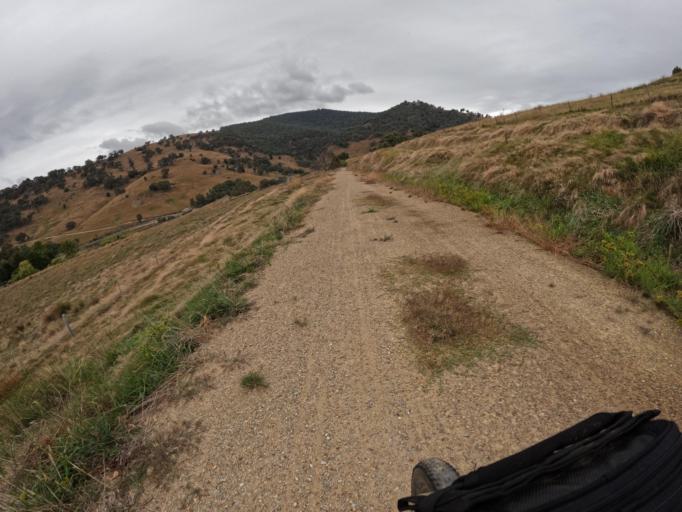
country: AU
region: New South Wales
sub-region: Albury Municipality
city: East Albury
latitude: -36.1849
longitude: 147.3666
